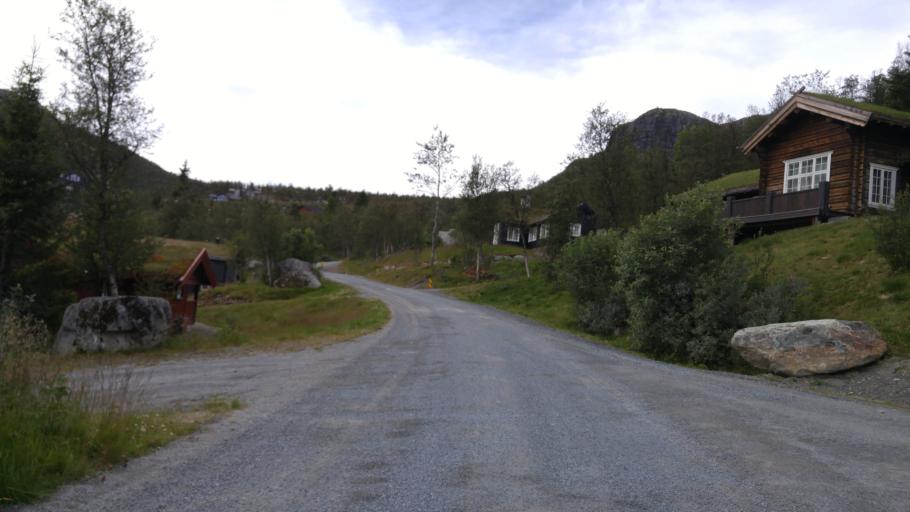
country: NO
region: Buskerud
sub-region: Hemsedal
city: Hemsedal
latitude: 60.8567
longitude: 8.4916
